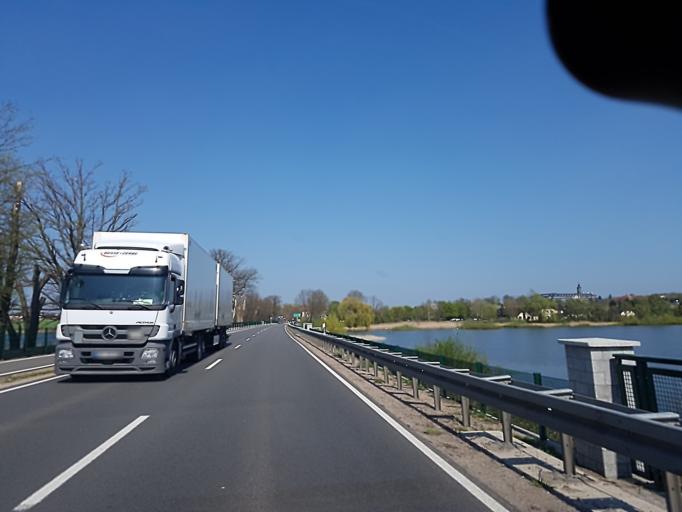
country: DE
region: Saxony
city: Wermsdorf
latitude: 51.2731
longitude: 12.9245
